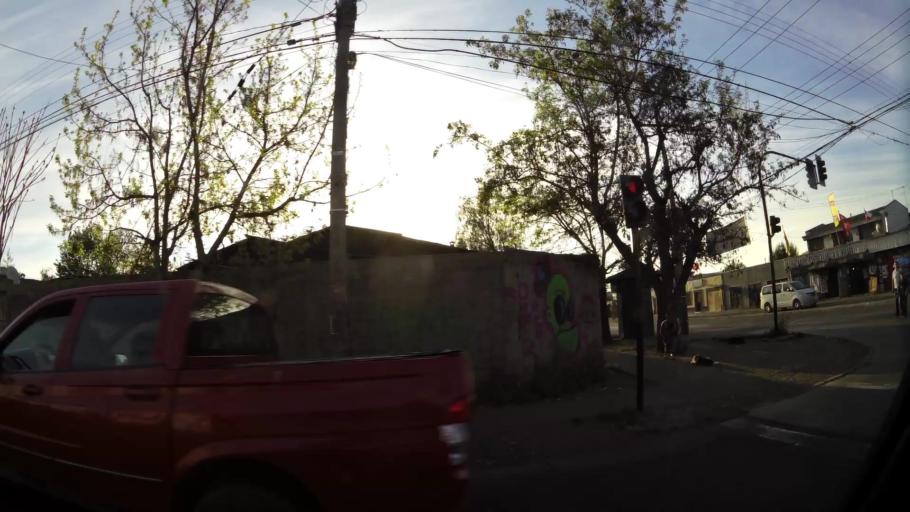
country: CL
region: Santiago Metropolitan
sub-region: Provincia de Santiago
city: Lo Prado
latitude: -33.4219
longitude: -70.7180
